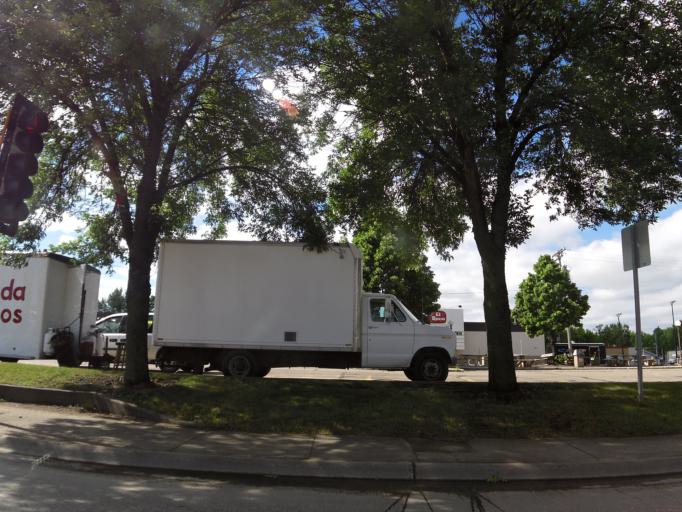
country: US
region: North Dakota
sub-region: Grand Forks County
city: Grand Forks
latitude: 47.9331
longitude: -97.0513
